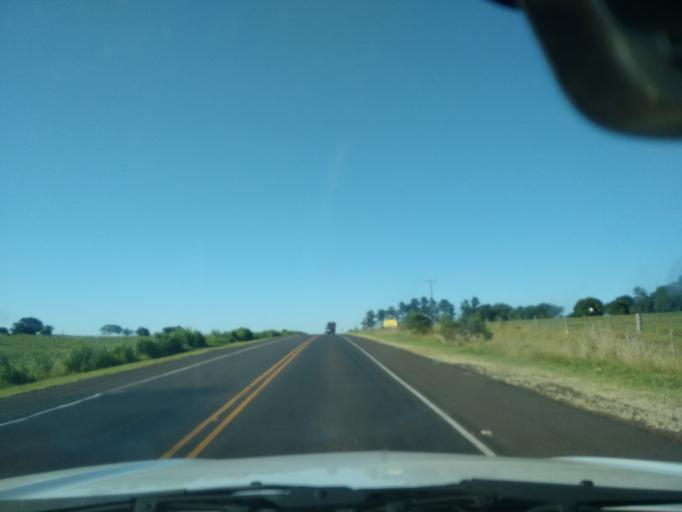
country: PY
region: Canindeyu
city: Salto del Guaira
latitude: -23.9761
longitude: -54.3309
